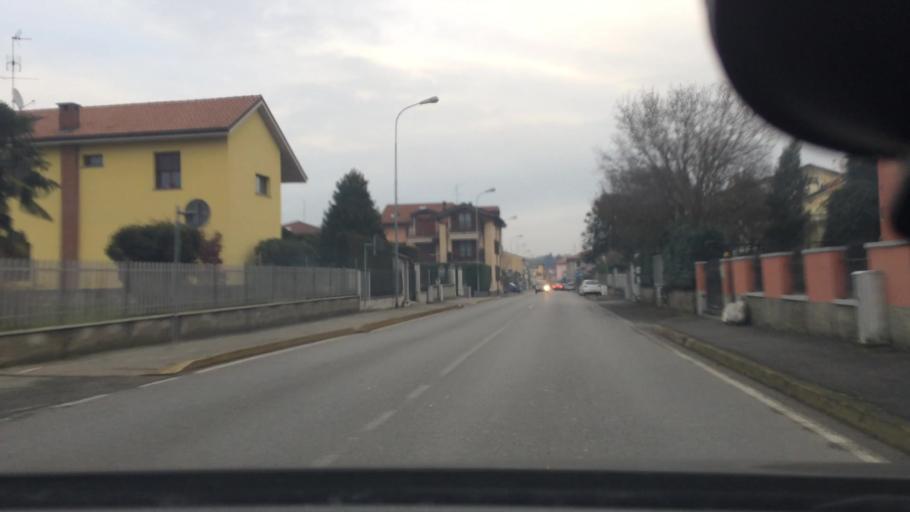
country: IT
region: Lombardy
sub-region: Provincia di Monza e Brianza
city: Ceriano Laghetto
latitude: 45.6286
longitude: 9.0739
